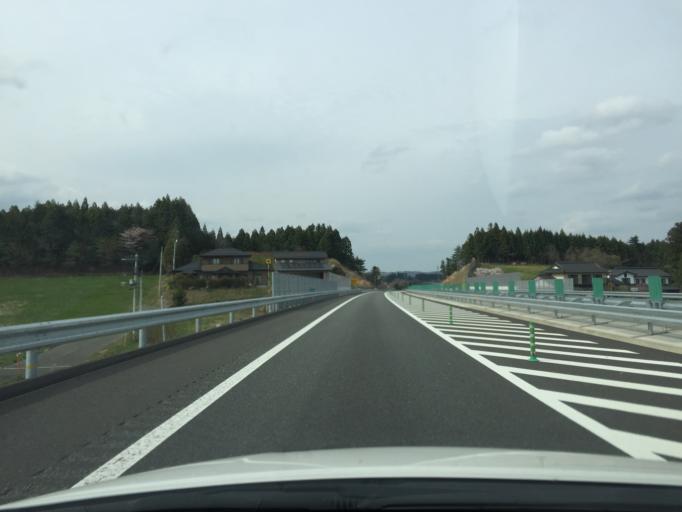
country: JP
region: Fukushima
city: Namie
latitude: 37.5354
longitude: 140.9407
